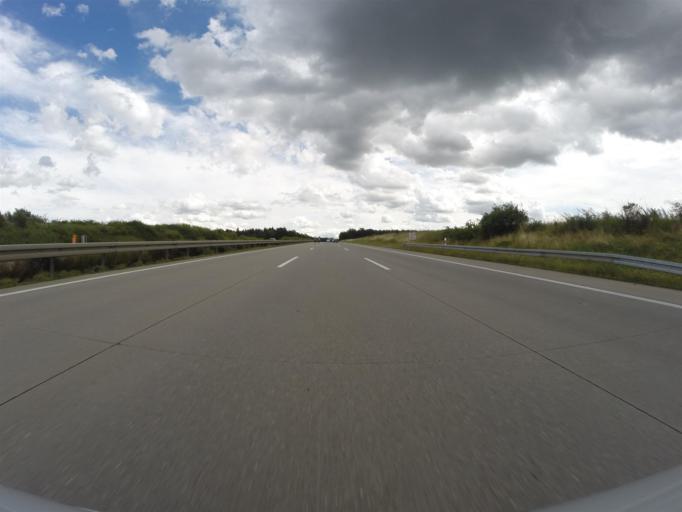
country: DE
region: Thuringia
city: Tautendorf
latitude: 50.8173
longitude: 11.8883
